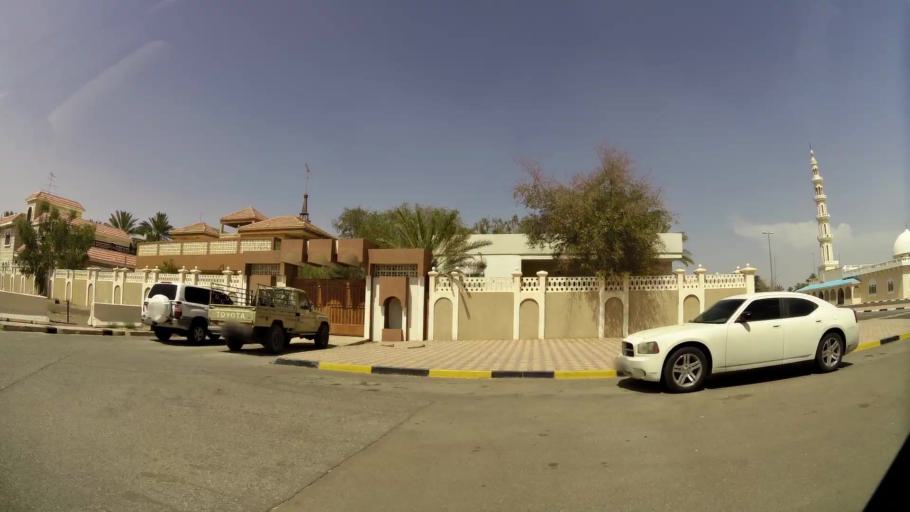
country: AE
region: Abu Dhabi
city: Al Ain
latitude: 24.2277
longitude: 55.7085
